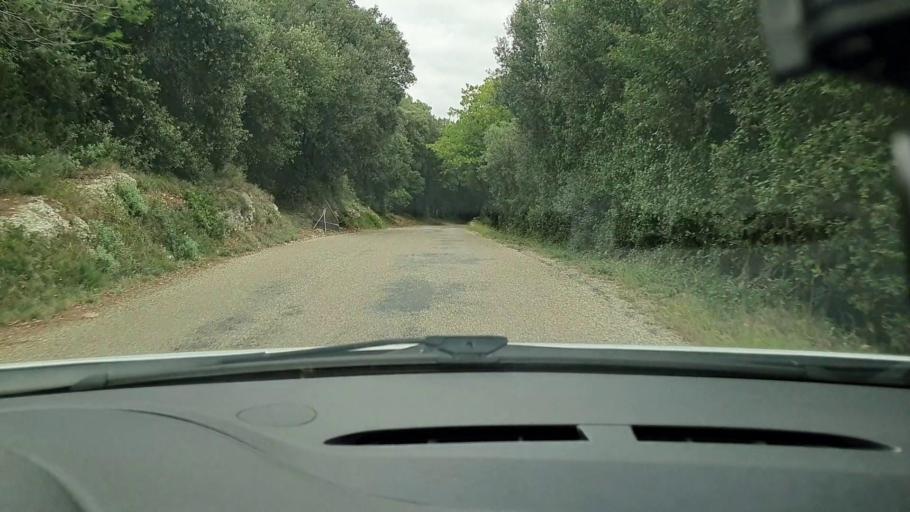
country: FR
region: Languedoc-Roussillon
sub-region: Departement du Gard
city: Montaren-et-Saint-Mediers
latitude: 44.0525
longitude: 4.3234
